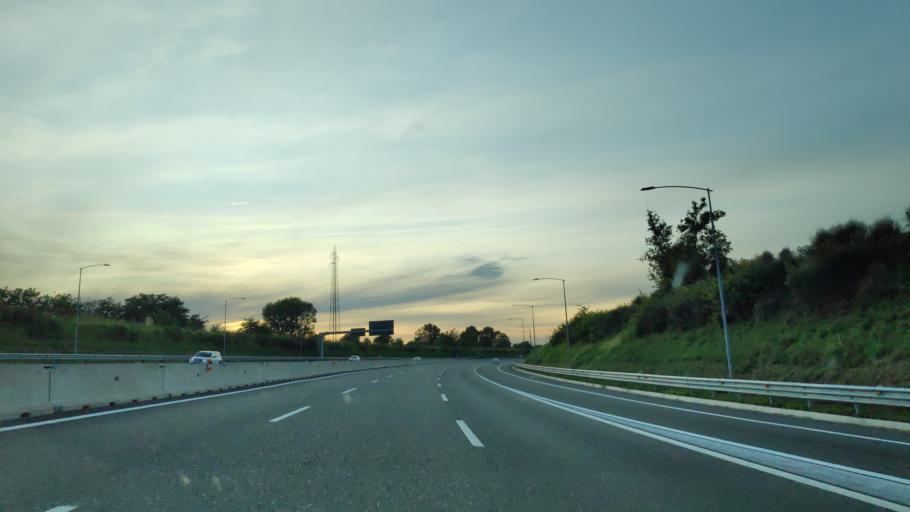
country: IT
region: Lombardy
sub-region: Citta metropolitana di Milano
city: Gorgonzola
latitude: 45.5481
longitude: 9.4146
